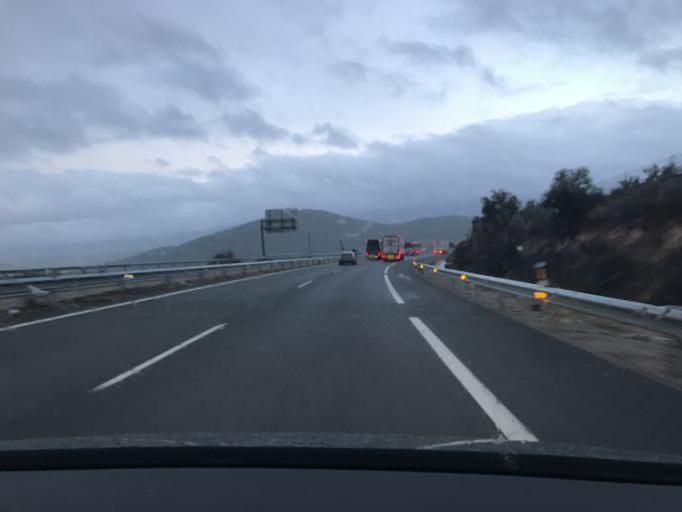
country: ES
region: Andalusia
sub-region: Provincia de Granada
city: Campotejar
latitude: 37.4645
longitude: -3.5642
